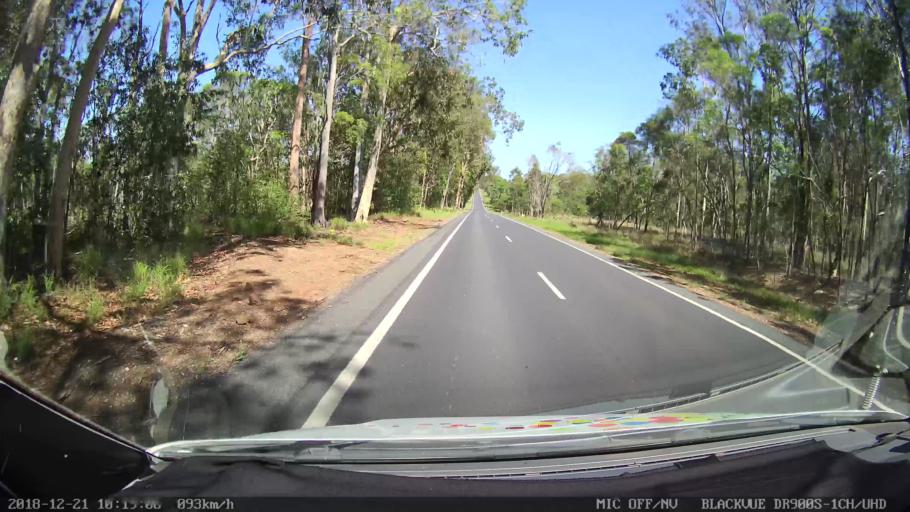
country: AU
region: New South Wales
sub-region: Clarence Valley
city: South Grafton
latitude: -29.6781
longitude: 152.8471
